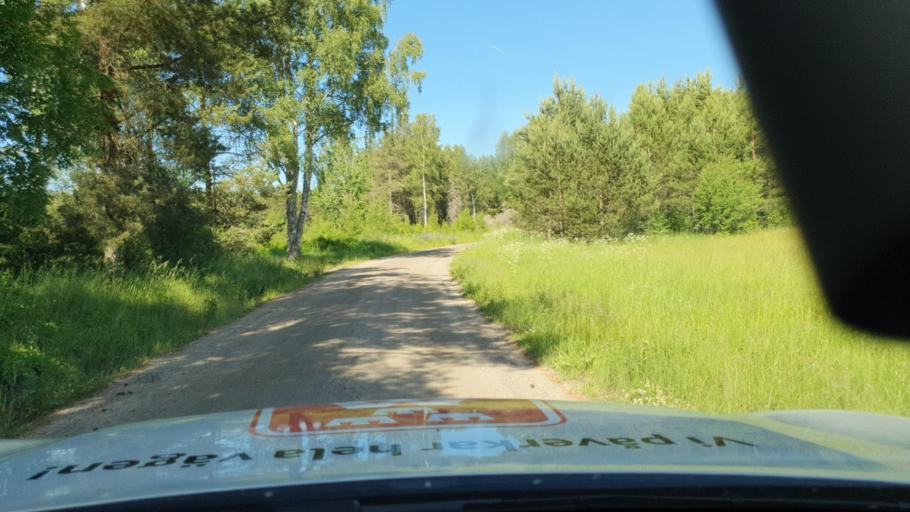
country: SE
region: Vaestra Goetaland
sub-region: Skovde Kommun
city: Skultorp
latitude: 58.3176
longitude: 13.8699
